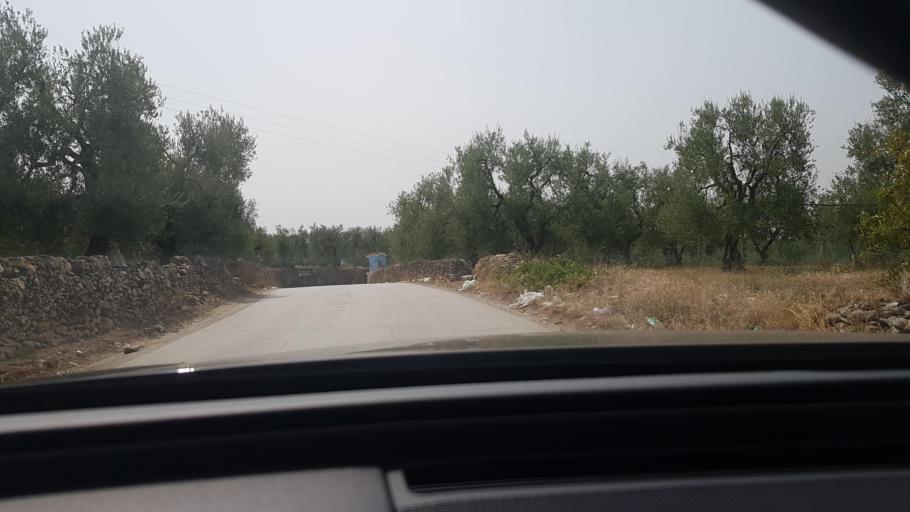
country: IT
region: Apulia
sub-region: Provincia di Barletta - Andria - Trani
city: Andria
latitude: 41.2269
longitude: 16.2682
